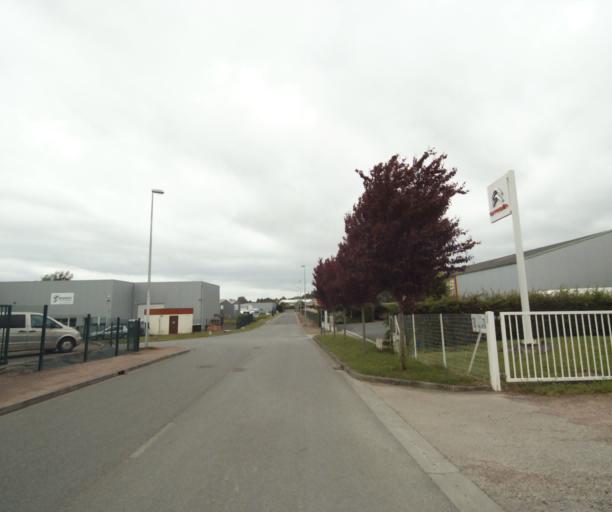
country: FR
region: Lower Normandy
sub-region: Departement du Calvados
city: Dives-sur-Mer
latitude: 49.2752
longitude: -0.0933
